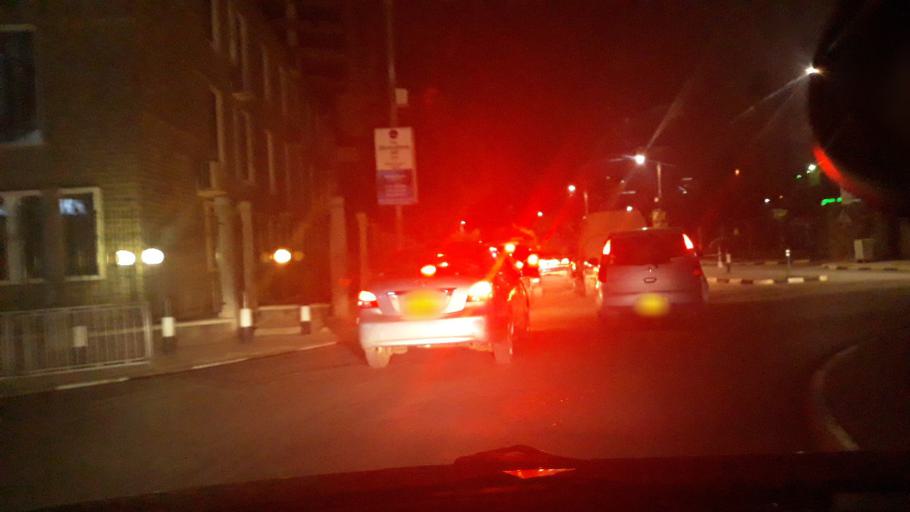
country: KE
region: Nairobi Area
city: Nairobi
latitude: -1.2906
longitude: 36.8213
